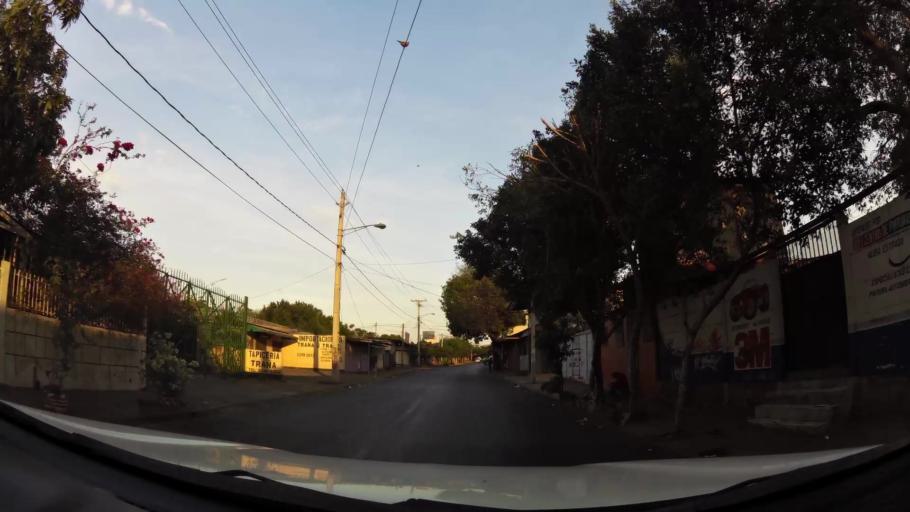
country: NI
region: Managua
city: Managua
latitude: 12.1428
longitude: -86.2569
